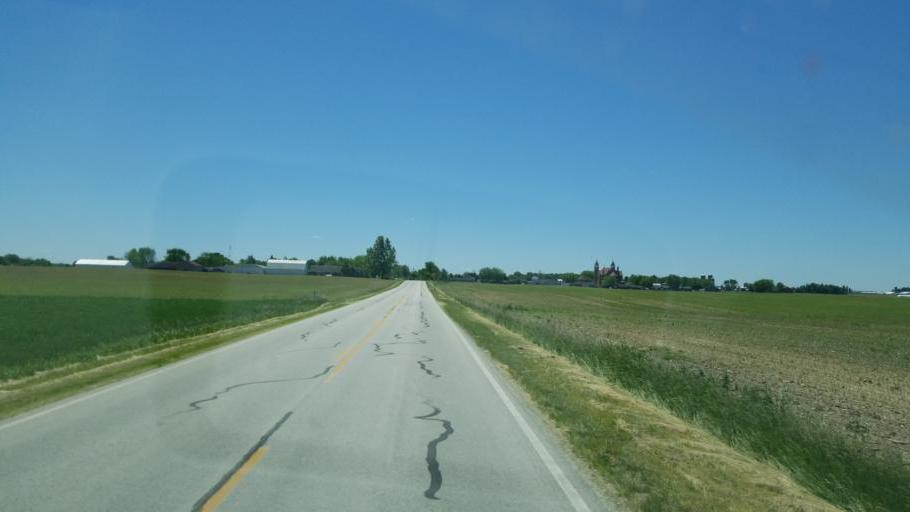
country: US
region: Ohio
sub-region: Mercer County
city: Saint Henry
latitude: 40.3596
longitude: -84.6433
